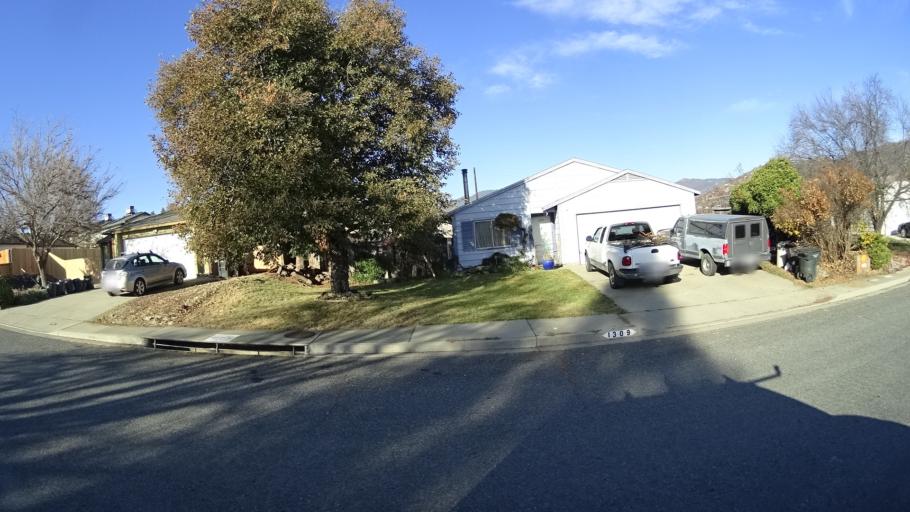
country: US
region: California
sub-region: Siskiyou County
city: Yreka
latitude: 41.7123
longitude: -122.6243
